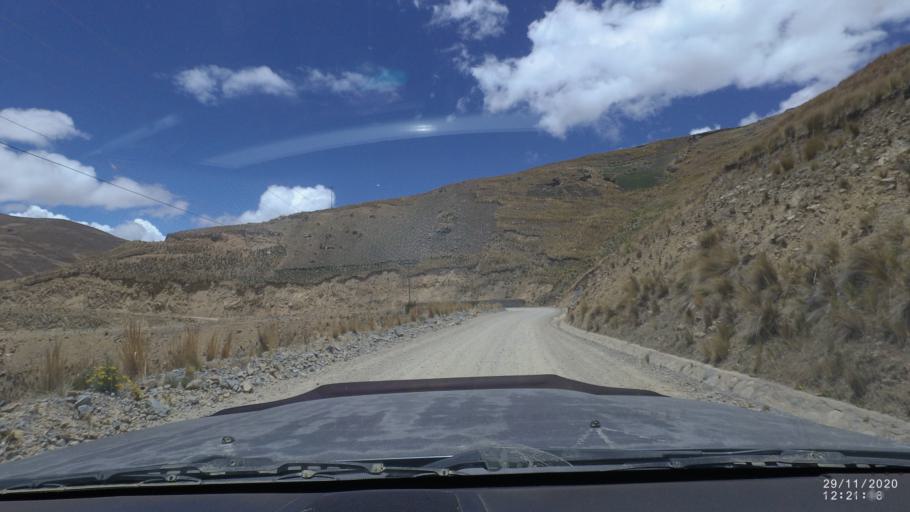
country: BO
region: Cochabamba
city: Cochabamba
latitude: -17.0979
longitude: -66.3262
